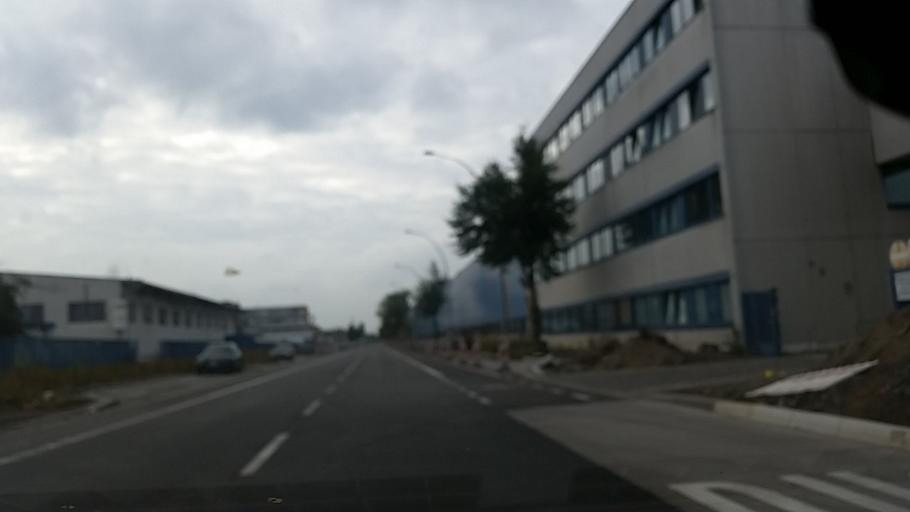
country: DE
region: Hamburg
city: Wandsbek
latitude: 53.5328
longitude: 10.0944
